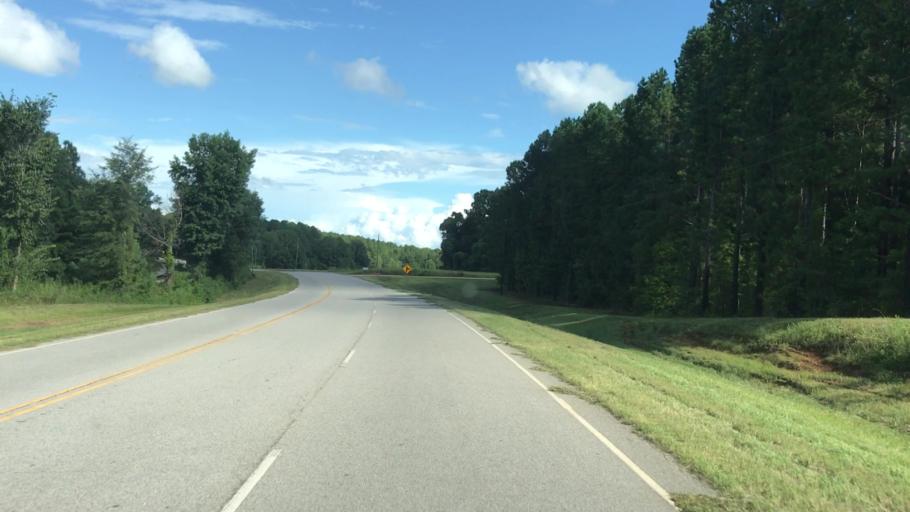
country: US
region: Georgia
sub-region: Warren County
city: Firing Range
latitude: 33.4864
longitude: -82.7951
